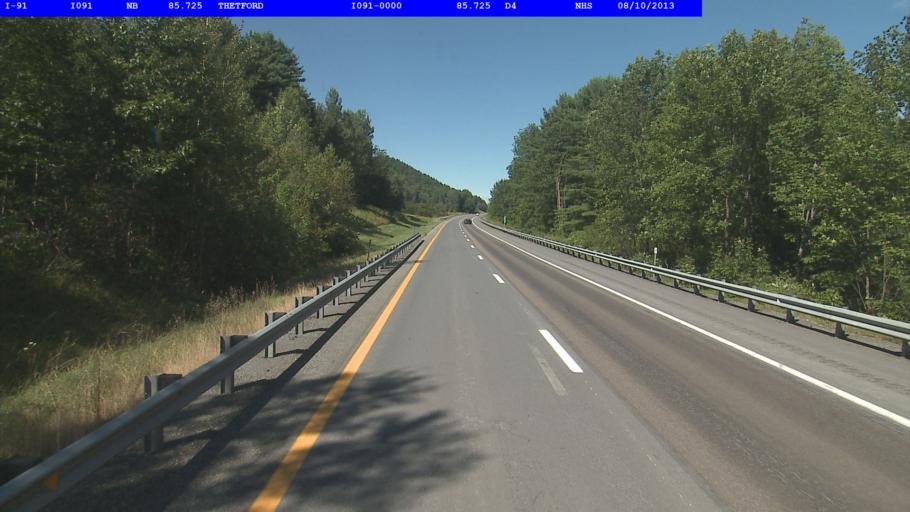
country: US
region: New Hampshire
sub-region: Grafton County
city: Lyme
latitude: 43.8330
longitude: -72.2057
